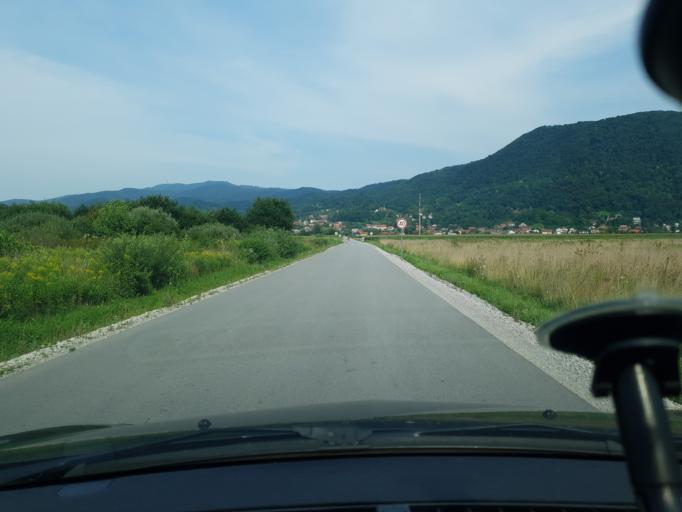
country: HR
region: Zagrebacka
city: Jablanovec
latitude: 45.8775
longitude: 15.8332
